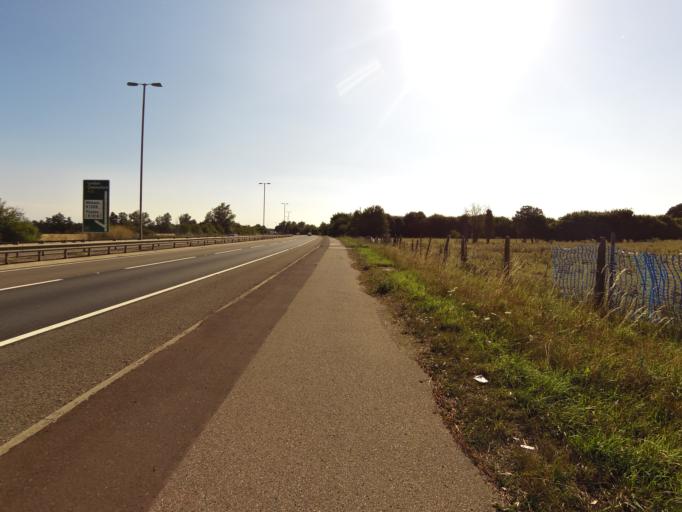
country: GB
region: England
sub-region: Essex
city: Witham
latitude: 51.8128
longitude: 0.6575
